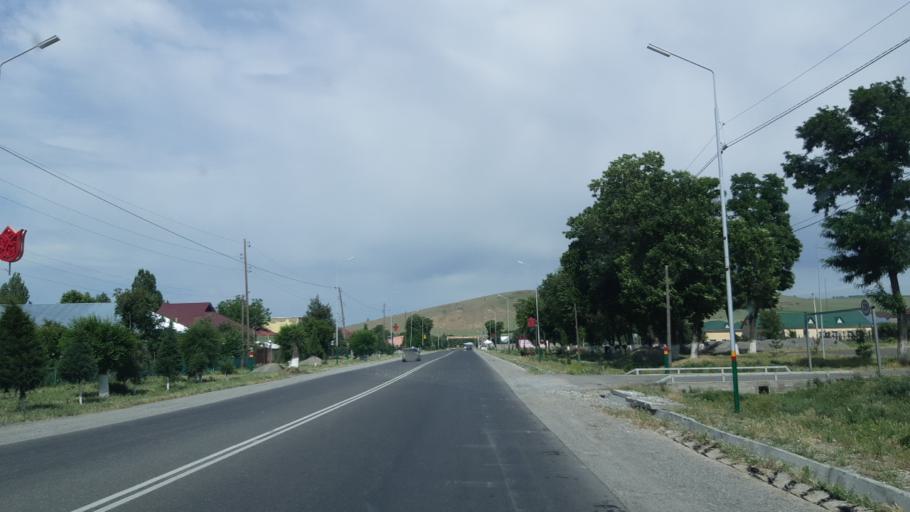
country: KZ
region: Ongtustik Qazaqstan
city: Turar Ryskulov
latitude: 42.5463
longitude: 70.3268
